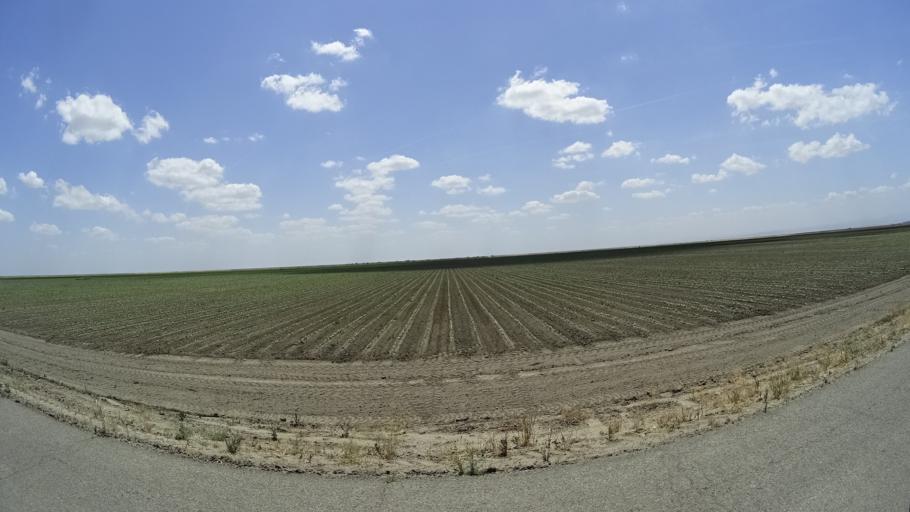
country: US
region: California
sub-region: Kings County
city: Stratford
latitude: 36.1527
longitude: -119.8142
